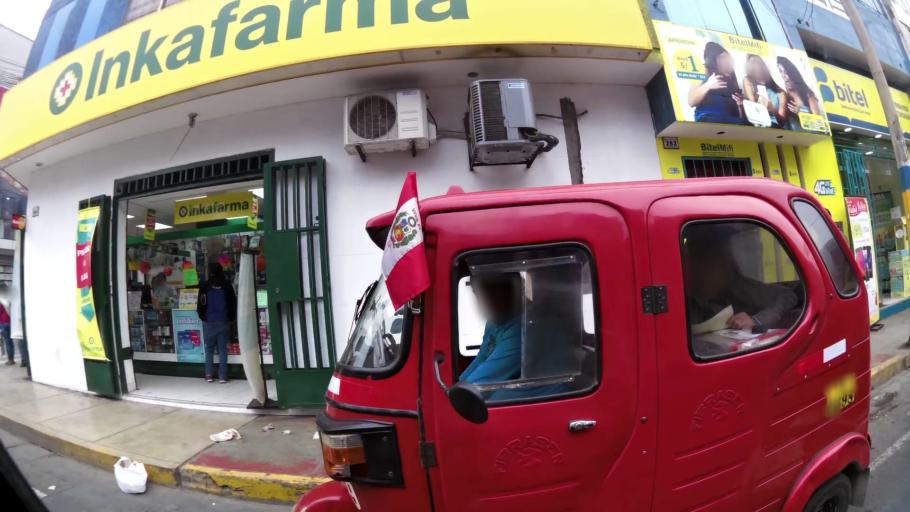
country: PE
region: Lima
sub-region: Barranca
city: Barranca
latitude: -10.7499
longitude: -77.7620
